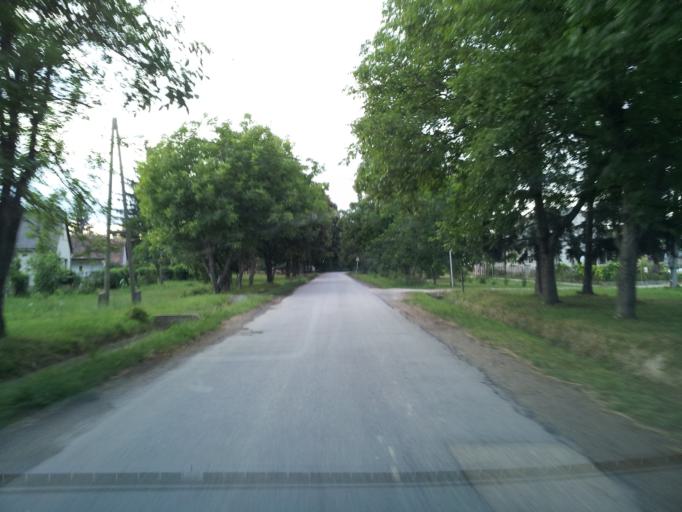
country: HU
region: Fejer
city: Lajoskomarom
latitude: 46.8190
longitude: 18.2798
